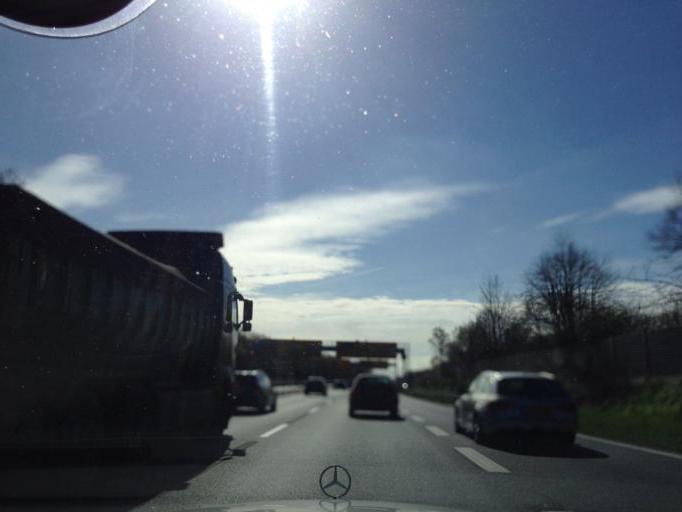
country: DE
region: Lower Saxony
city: Laatzen
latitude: 52.3359
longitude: 9.8072
